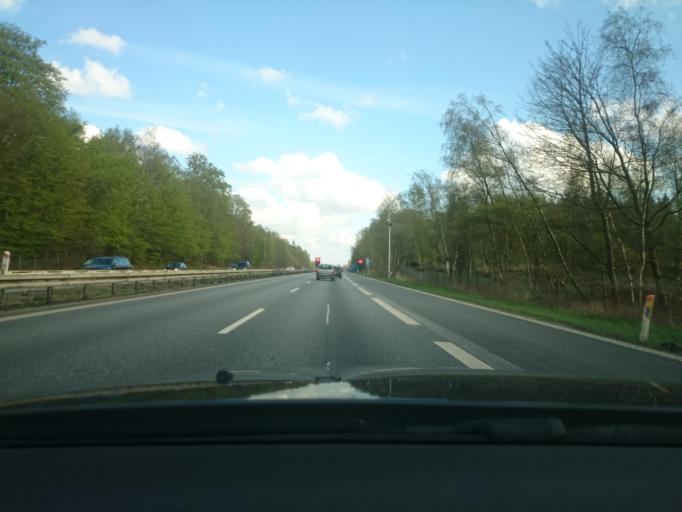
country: DK
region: Capital Region
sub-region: Fureso Kommune
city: Stavnsholt
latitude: 55.7700
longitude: 12.4242
